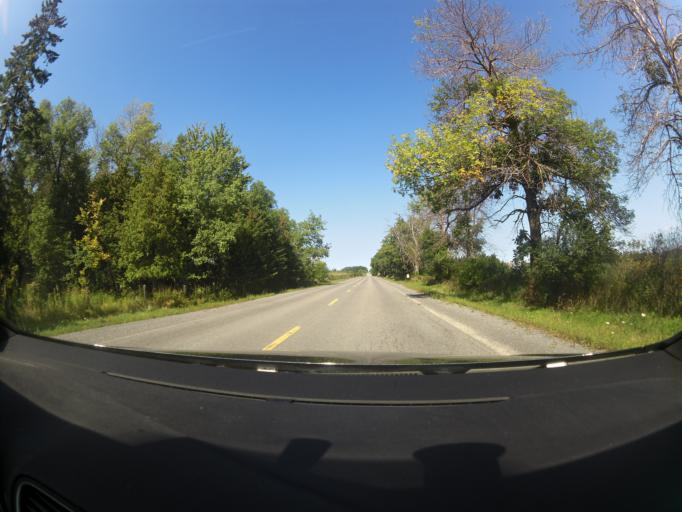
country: CA
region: Ontario
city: Arnprior
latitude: 45.3736
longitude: -76.2609
